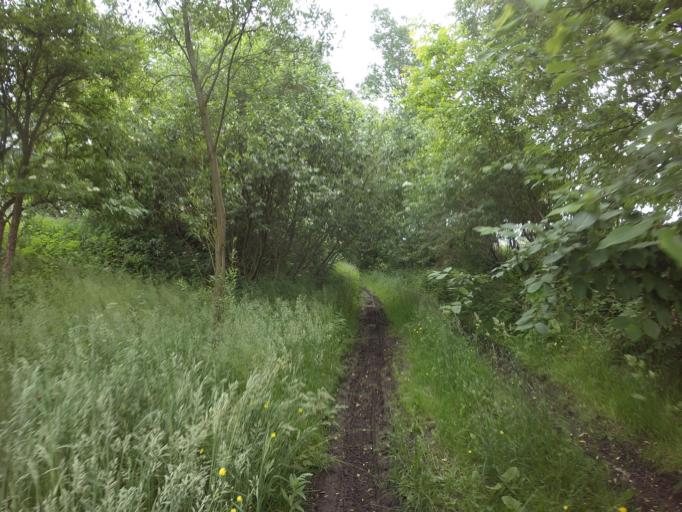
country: PL
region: West Pomeranian Voivodeship
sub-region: Powiat stargardzki
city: Dobrzany
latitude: 53.3219
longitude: 15.4945
